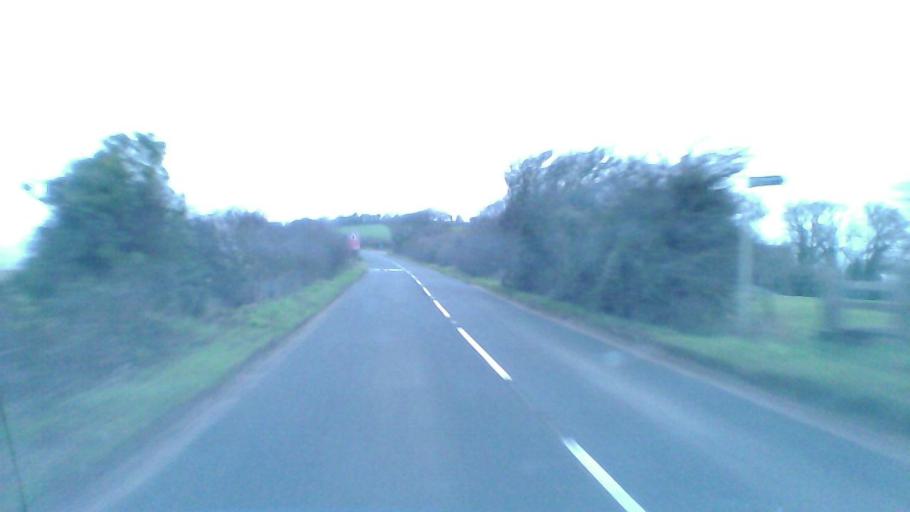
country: GB
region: England
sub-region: Isle of Wight
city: Newchurch
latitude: 50.6825
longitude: -1.2176
